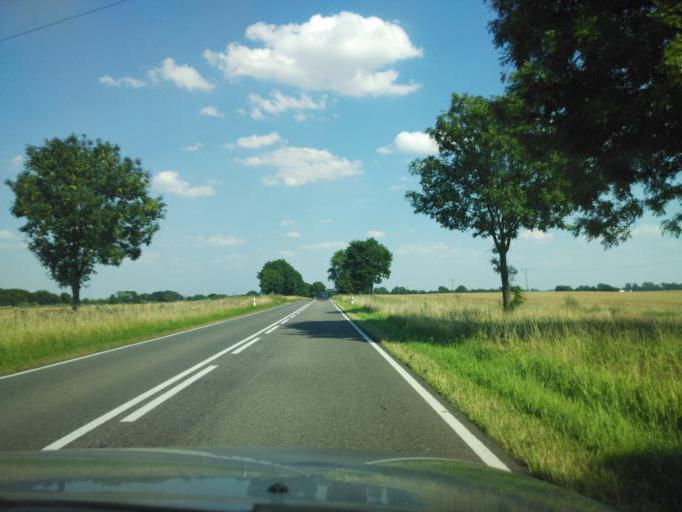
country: PL
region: West Pomeranian Voivodeship
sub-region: Powiat pyrzycki
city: Kozielice
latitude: 53.1225
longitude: 14.7837
